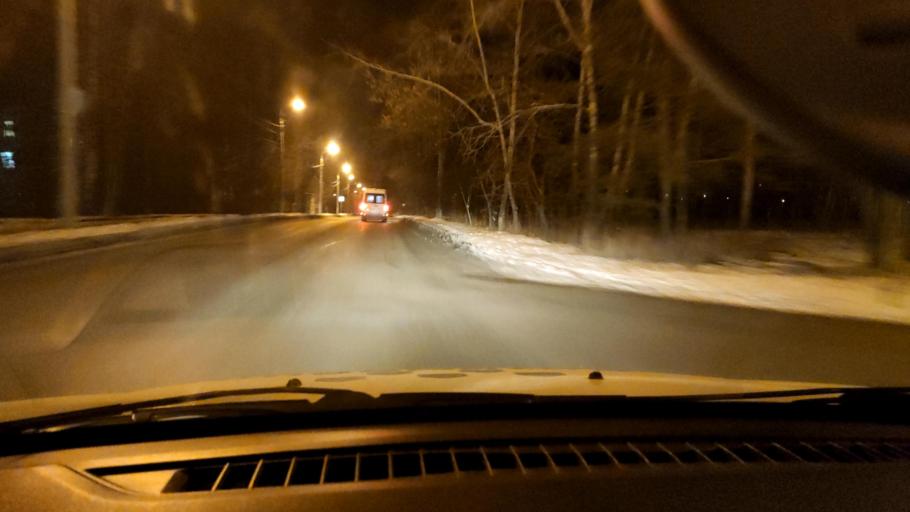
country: RU
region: Perm
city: Overyata
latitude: 58.0247
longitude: 55.8475
